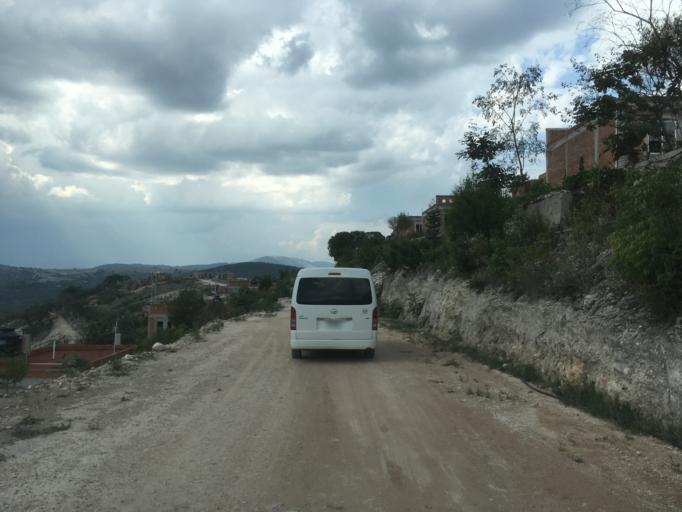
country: MX
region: Oaxaca
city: Santiago Tilantongo
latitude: 17.2207
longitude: -97.2716
